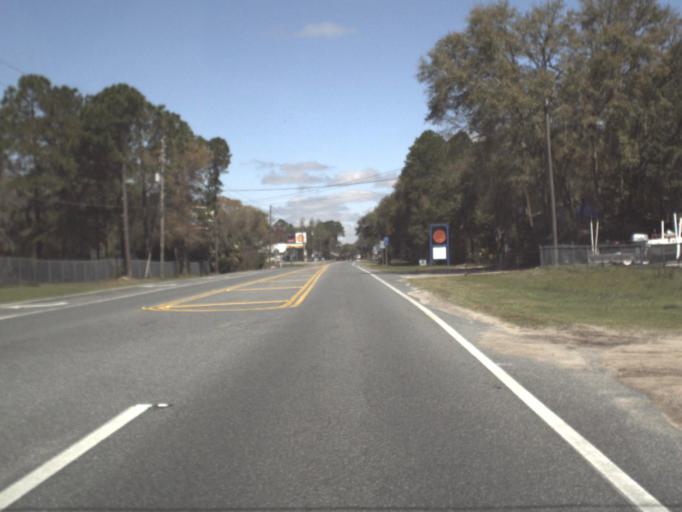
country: US
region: Florida
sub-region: Wakulla County
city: Crawfordville
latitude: 30.0802
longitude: -84.3887
